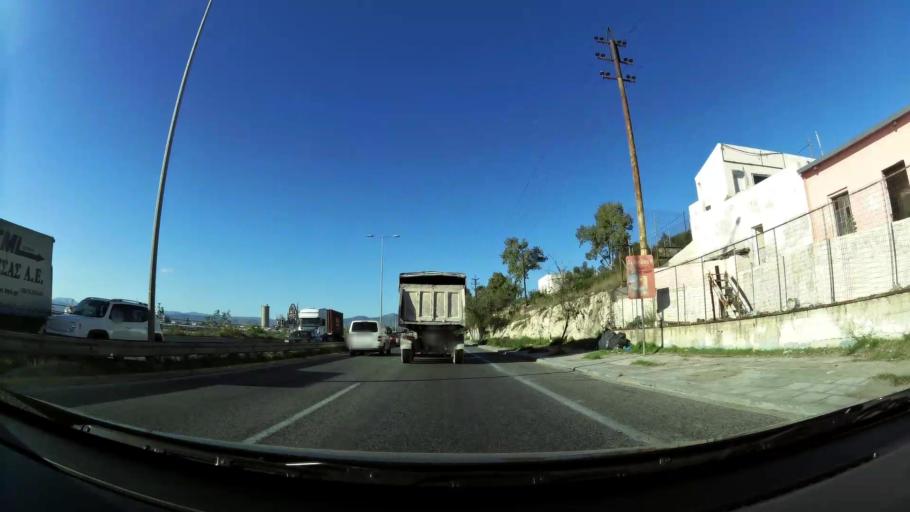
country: GR
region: Attica
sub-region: Nomarchia Athinas
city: Skaramangas
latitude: 38.0267
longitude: 23.5983
